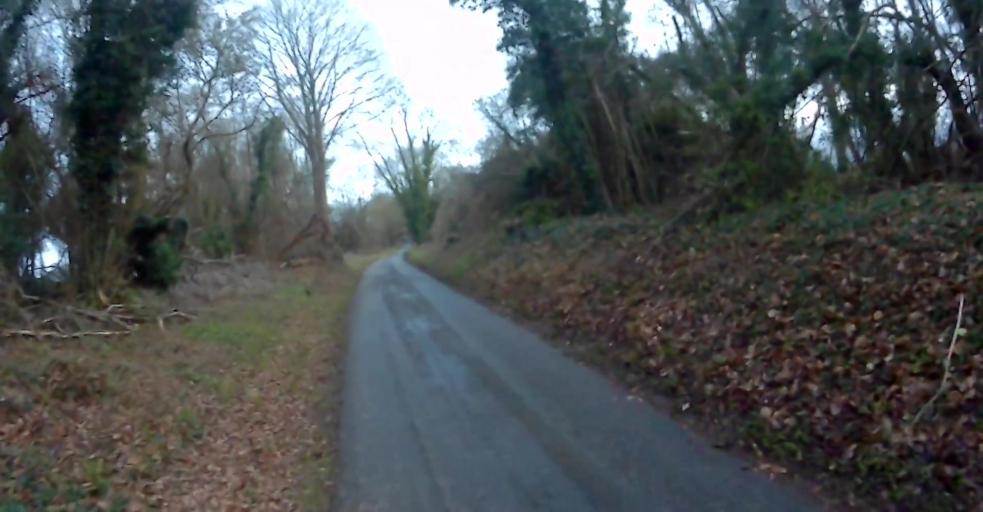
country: GB
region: England
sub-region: Hampshire
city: Overton
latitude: 51.2565
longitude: -1.2280
